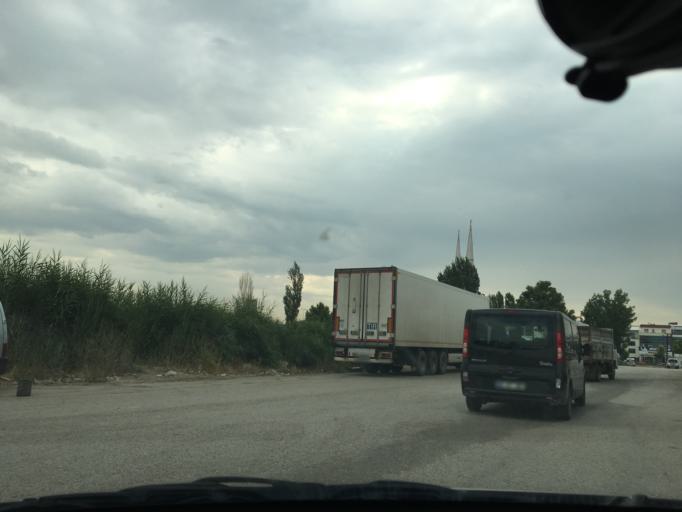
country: TR
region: Ankara
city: Batikent
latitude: 39.9353
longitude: 32.7106
